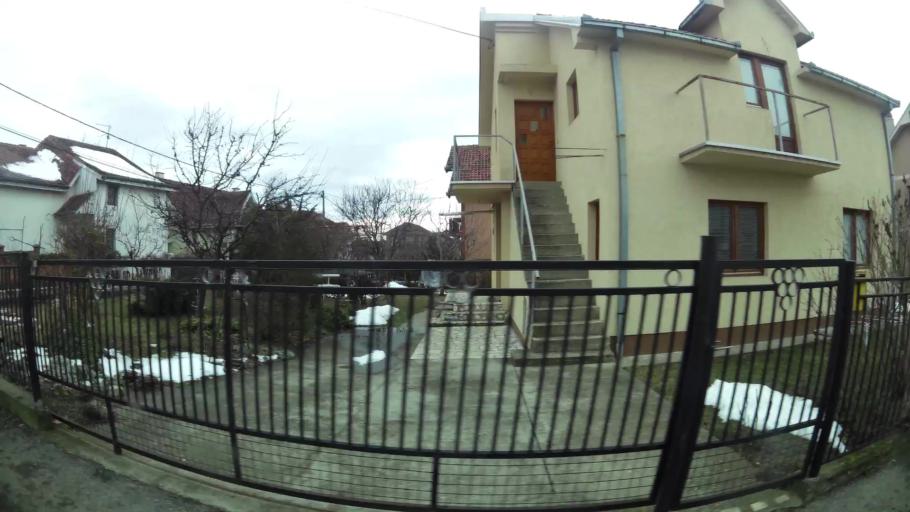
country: RS
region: Central Serbia
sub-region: Belgrade
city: Rakovica
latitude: 44.7412
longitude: 20.3977
